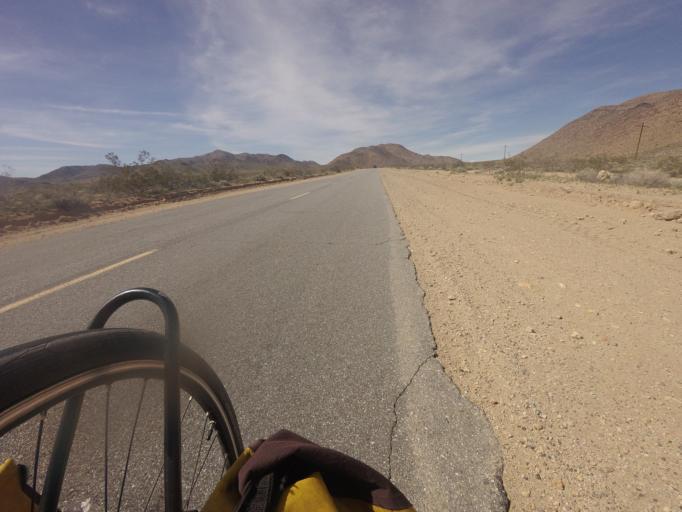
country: US
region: California
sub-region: San Bernardino County
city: Searles Valley
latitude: 35.5764
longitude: -117.4535
